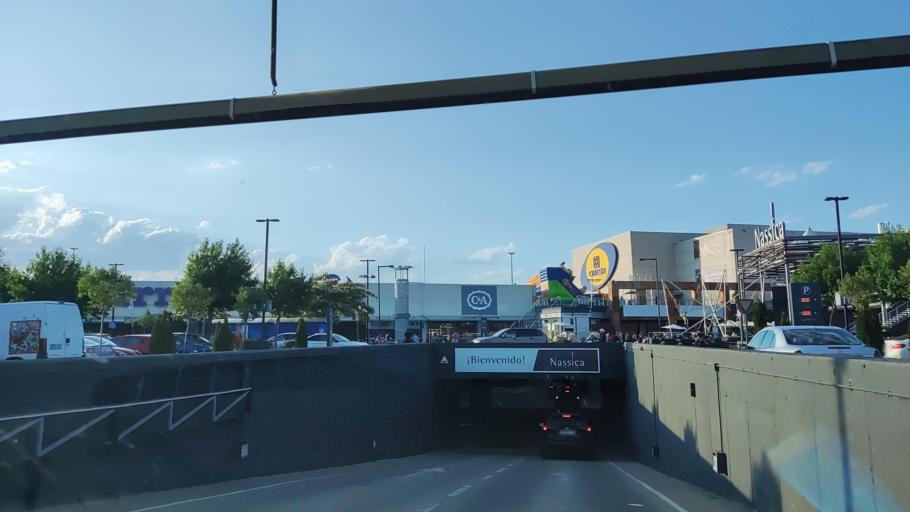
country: ES
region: Madrid
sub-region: Provincia de Madrid
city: Pinto
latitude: 40.2714
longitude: -3.6975
